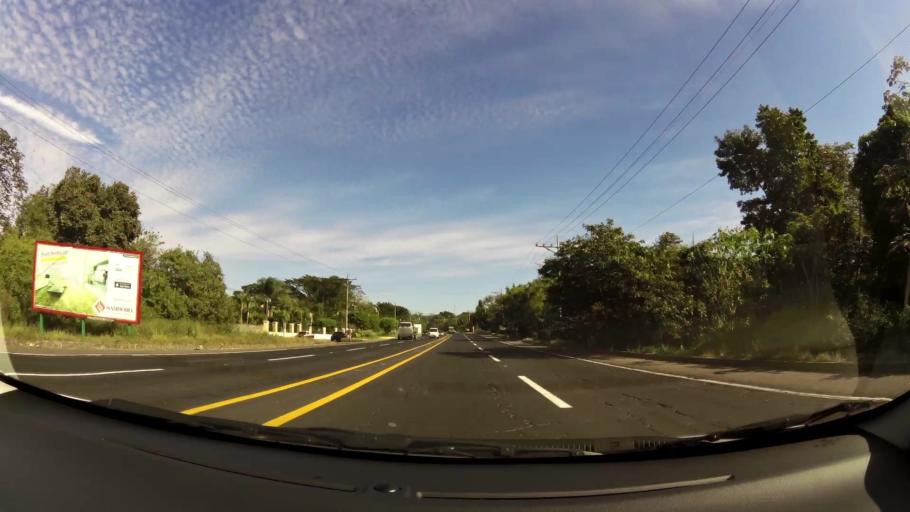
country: SV
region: Santa Ana
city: Santa Ana
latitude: 13.9865
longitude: -89.6046
